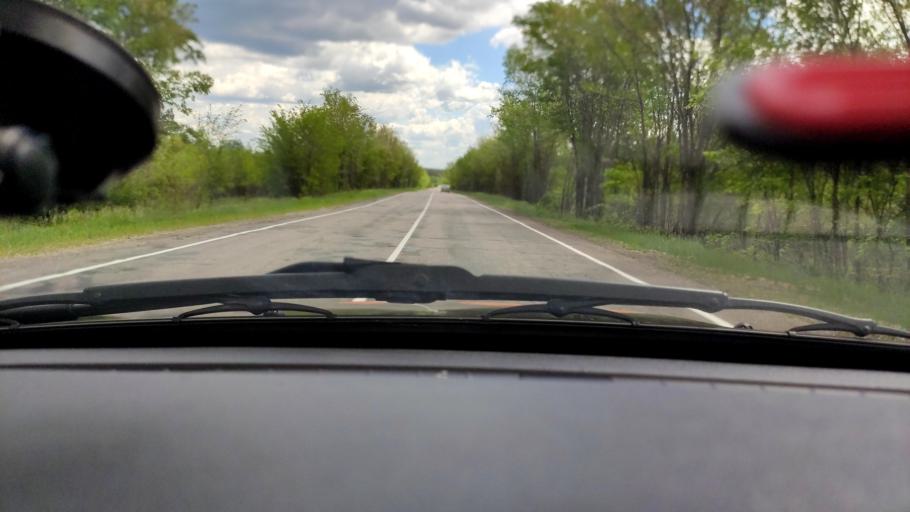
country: RU
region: Belgorod
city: Krasnoye
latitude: 51.0636
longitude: 38.8225
